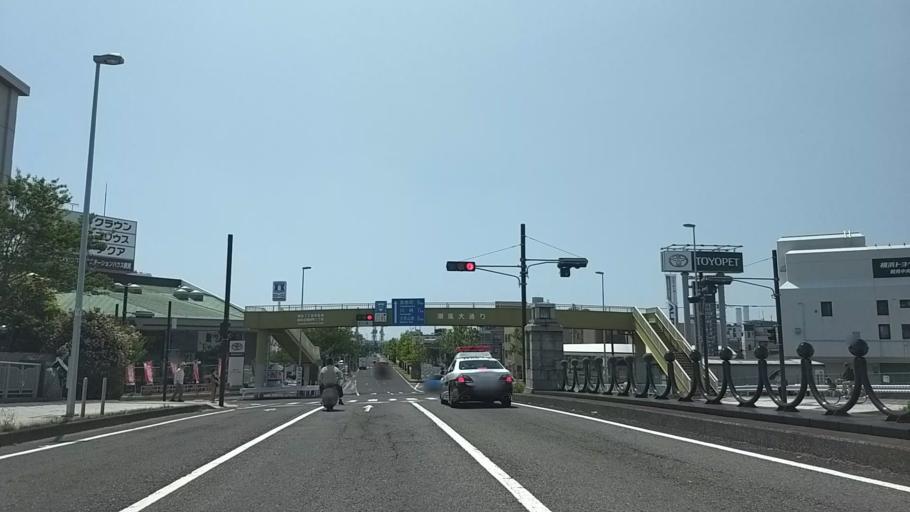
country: JP
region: Kanagawa
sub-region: Kawasaki-shi
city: Kawasaki
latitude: 35.5059
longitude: 139.6841
